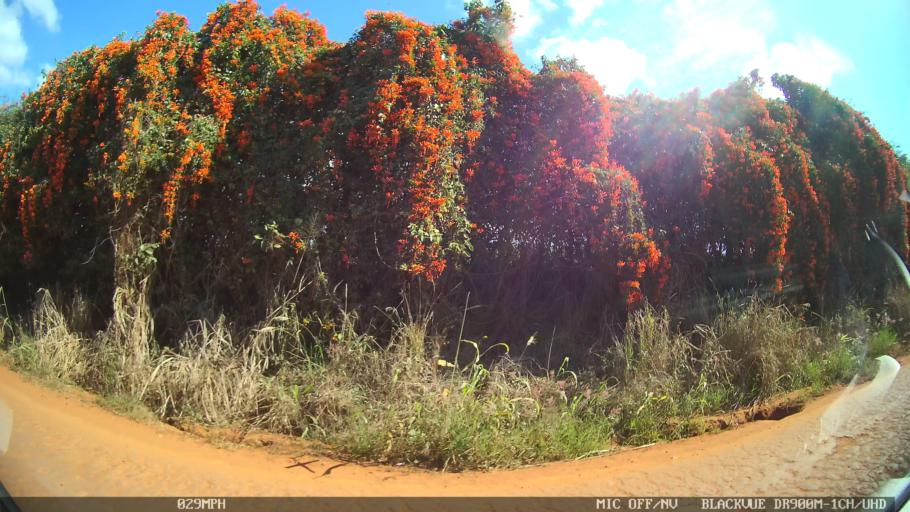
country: BR
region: Sao Paulo
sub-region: Sumare
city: Sumare
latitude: -22.8515
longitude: -47.2927
